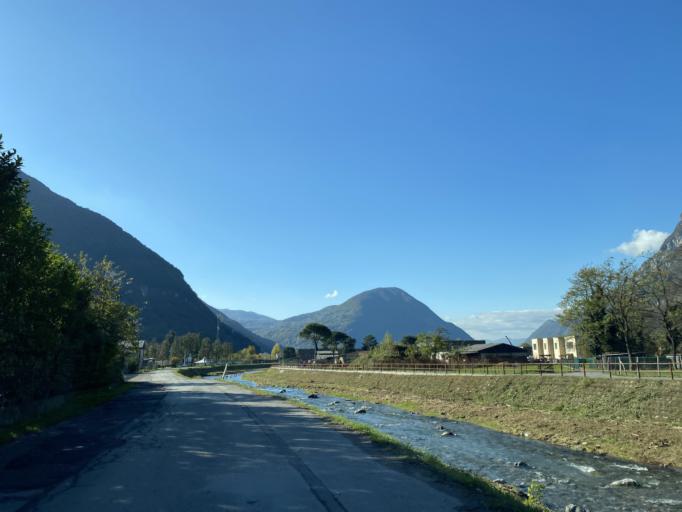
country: IT
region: Lombardy
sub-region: Provincia di Como
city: Porlezza
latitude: 46.0330
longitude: 9.1342
